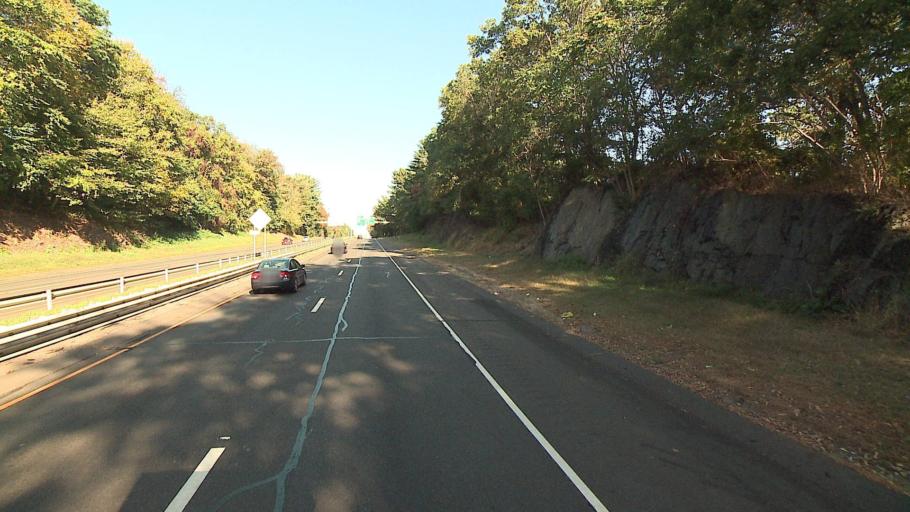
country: US
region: Connecticut
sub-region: New Haven County
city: City of Milford (balance)
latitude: 41.2381
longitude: -73.0758
